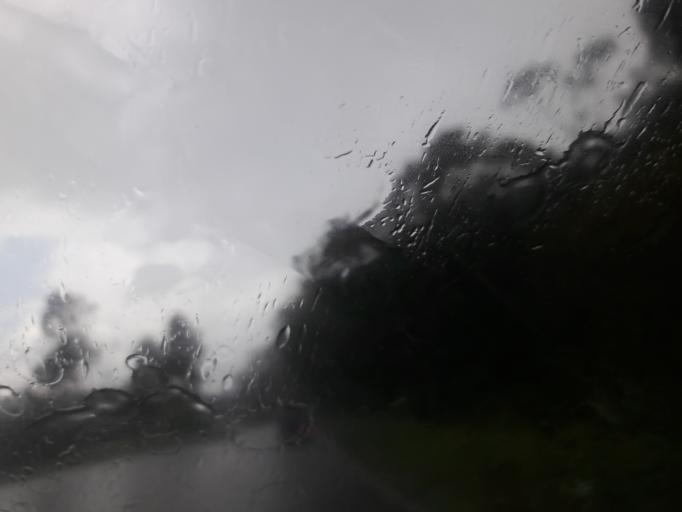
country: BR
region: Sao Paulo
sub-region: Bom Jesus Dos Perdoes
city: Bom Jesus dos Perdoes
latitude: -23.2334
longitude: -46.4090
